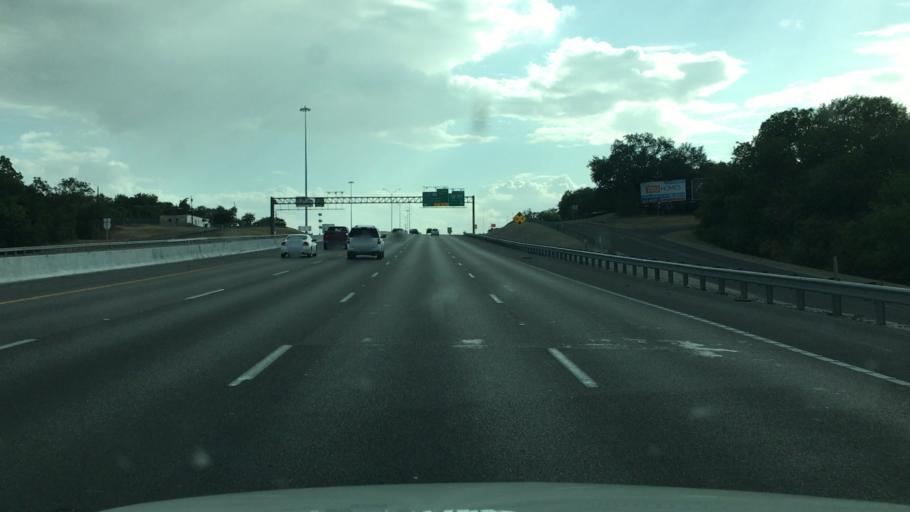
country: US
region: Texas
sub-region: Bell County
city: Belton
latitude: 31.0510
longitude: -97.4597
